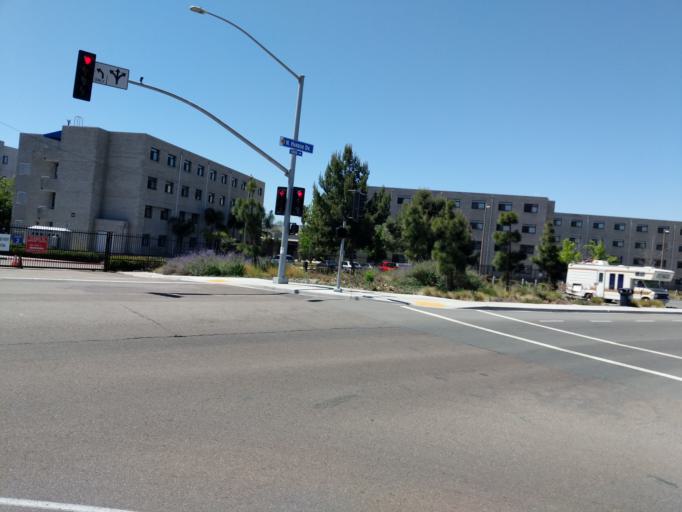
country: US
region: California
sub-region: San Diego County
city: Coronado
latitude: 32.7257
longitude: -117.2214
